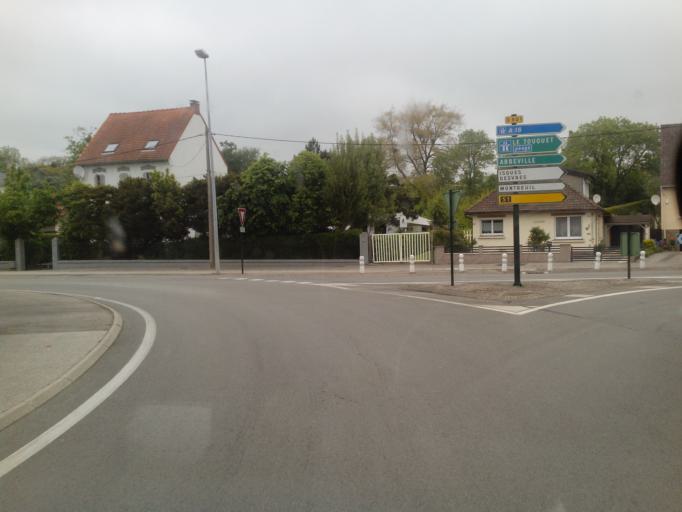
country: FR
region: Nord-Pas-de-Calais
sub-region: Departement du Pas-de-Calais
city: Saint-Etienne-au-Mont
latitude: 50.6832
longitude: 1.6329
